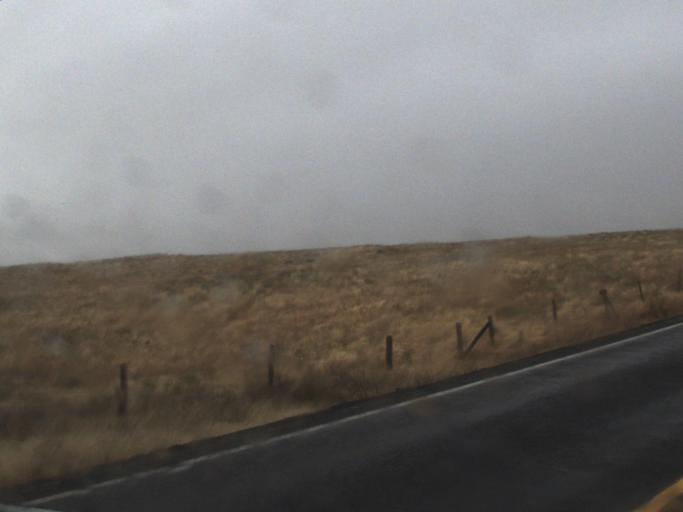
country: US
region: Washington
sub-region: Spokane County
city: Medical Lake
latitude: 47.2337
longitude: -117.9139
